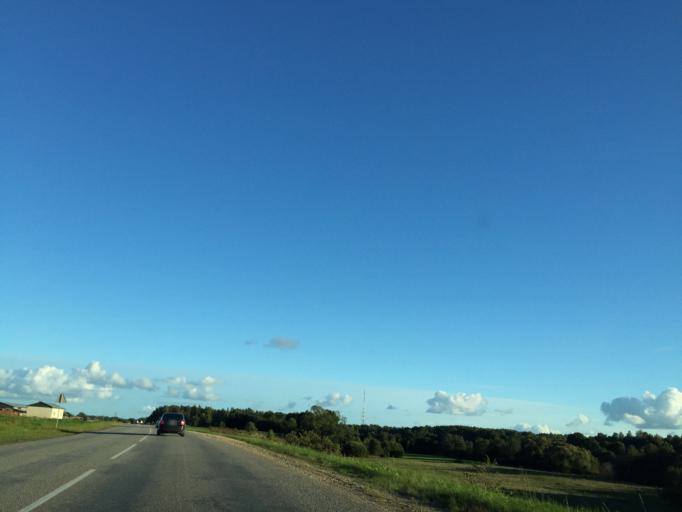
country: LV
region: Kuldigas Rajons
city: Kuldiga
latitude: 56.9583
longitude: 22.0044
